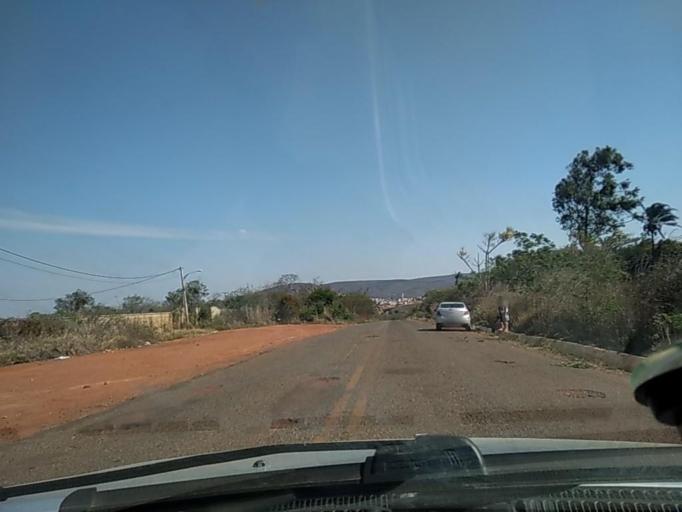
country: BR
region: Bahia
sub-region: Caetite
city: Caetite
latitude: -14.0343
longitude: -42.4869
